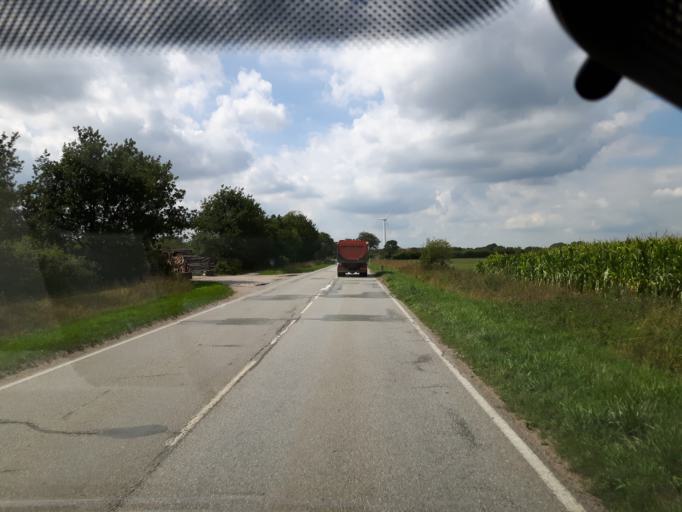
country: DE
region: Schleswig-Holstein
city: Harrislee
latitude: 54.8028
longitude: 9.3610
